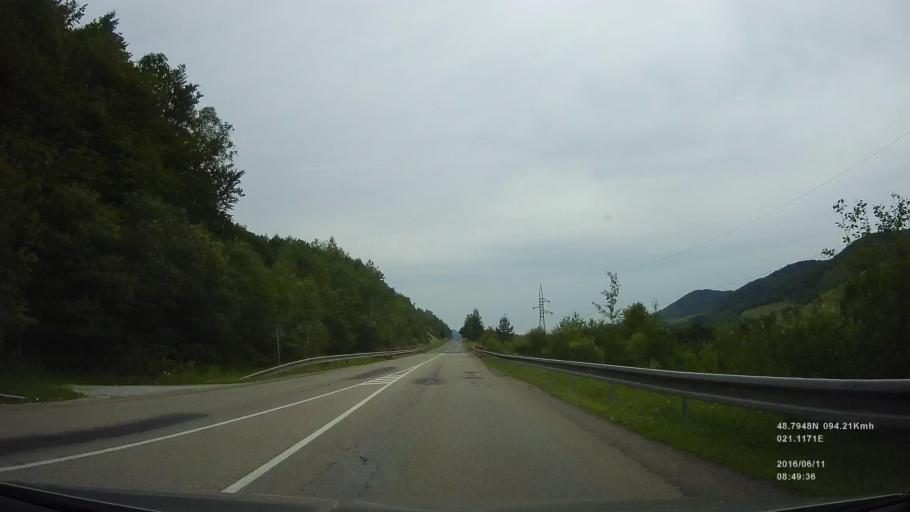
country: SK
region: Kosicky
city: Kosice
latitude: 48.7893
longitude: 21.1248
